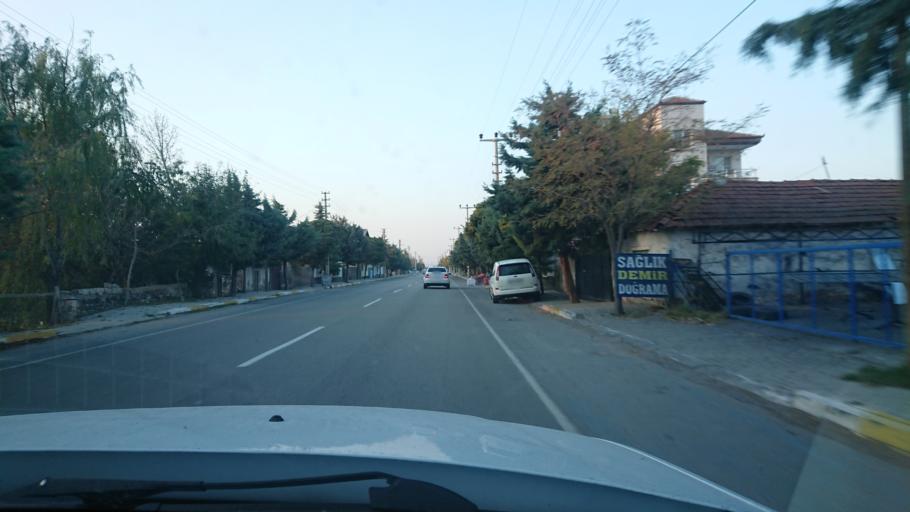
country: TR
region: Aksaray
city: Aksaray
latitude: 38.3053
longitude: 34.0685
